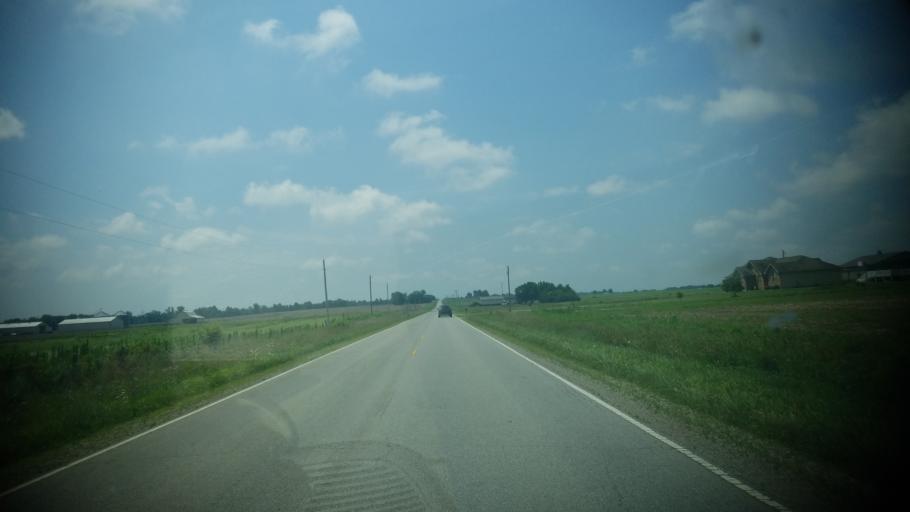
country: US
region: Illinois
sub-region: Wayne County
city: Fairfield
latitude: 38.4489
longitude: -88.3492
